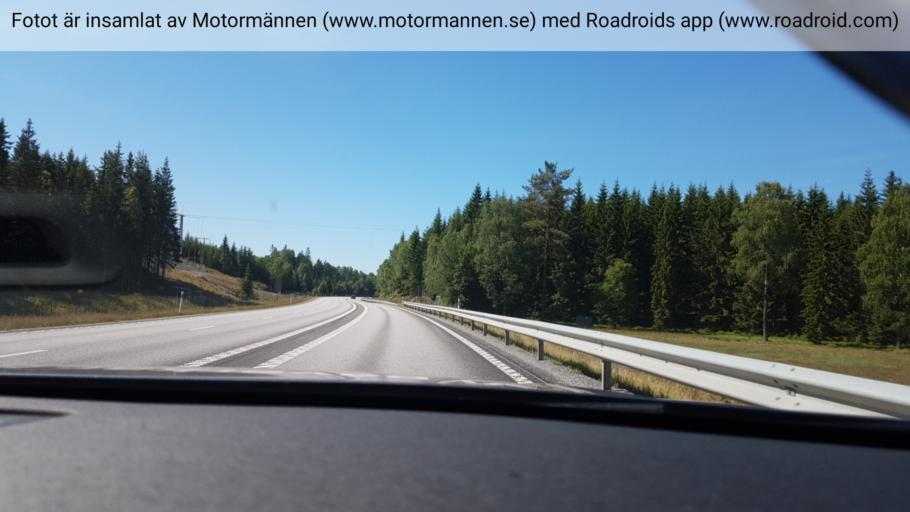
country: SE
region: Vaestra Goetaland
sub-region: Boras Kommun
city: Viskafors
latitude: 57.6383
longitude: 12.9015
